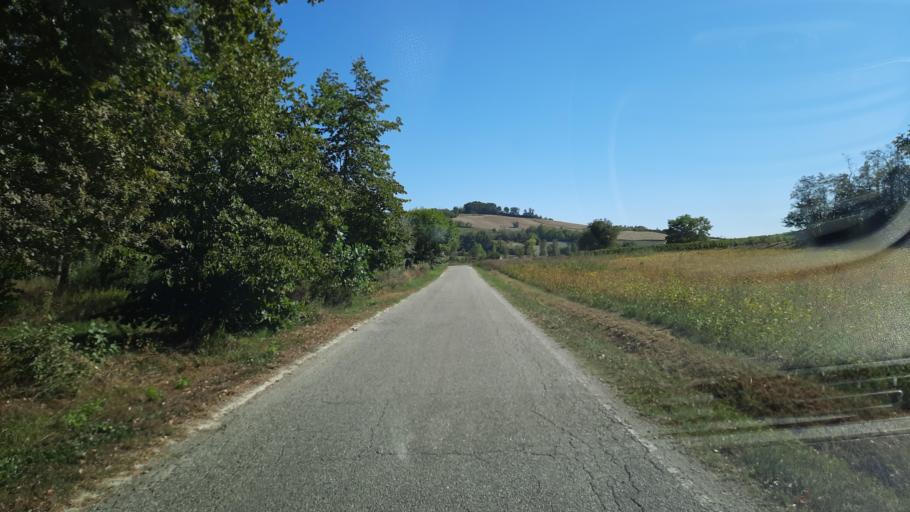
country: IT
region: Piedmont
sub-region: Provincia di Alessandria
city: Cuccaro Monferrato
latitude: 44.9994
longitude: 8.4413
